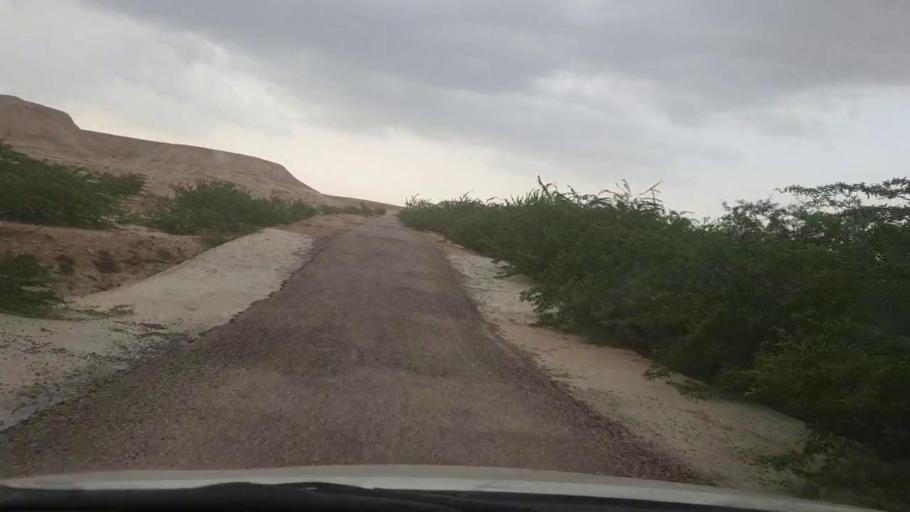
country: PK
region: Sindh
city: Khairpur
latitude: 27.4679
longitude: 68.9200
